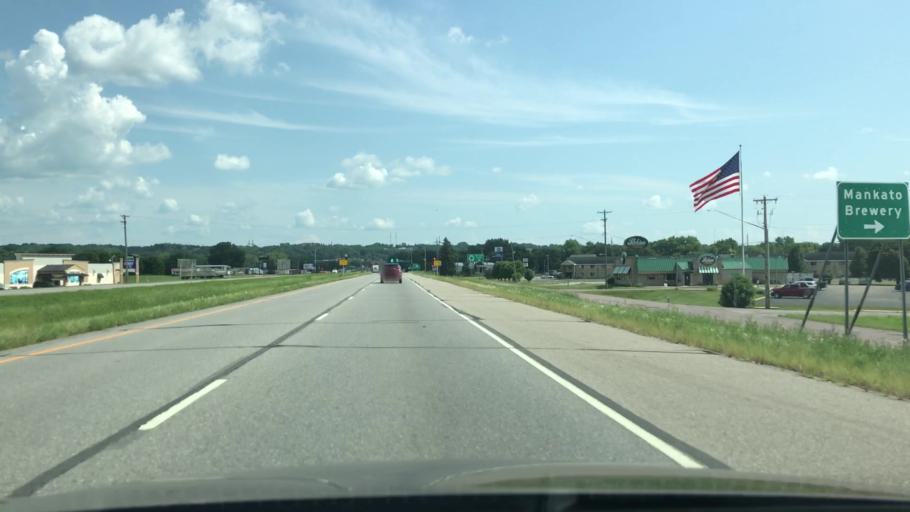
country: US
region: Minnesota
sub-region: Blue Earth County
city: Mankato
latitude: 44.1845
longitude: -94.0108
